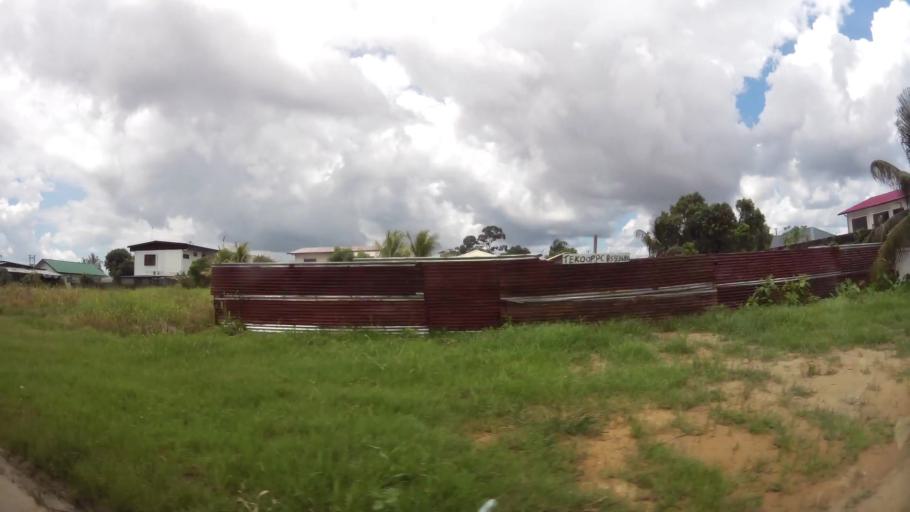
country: SR
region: Paramaribo
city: Paramaribo
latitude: 5.8603
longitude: -55.1333
